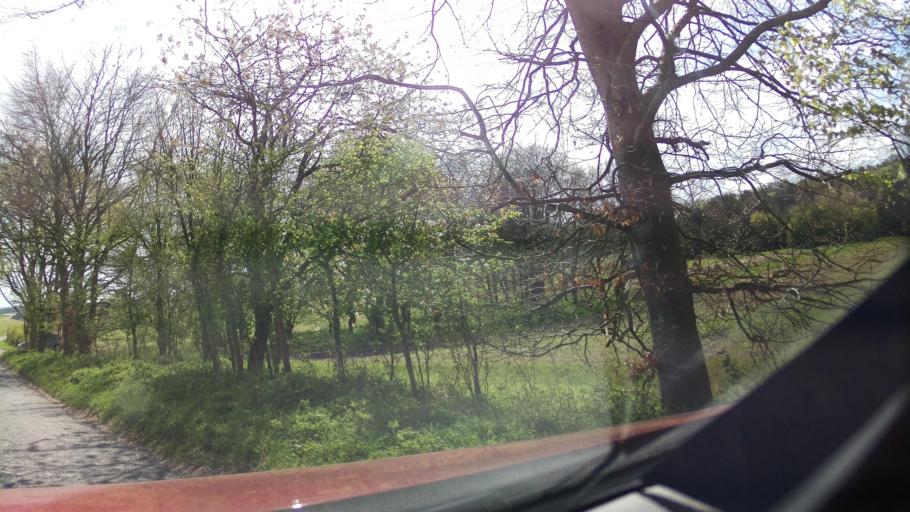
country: GB
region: England
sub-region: West Berkshire
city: Kintbury
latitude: 51.3379
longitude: -1.4700
